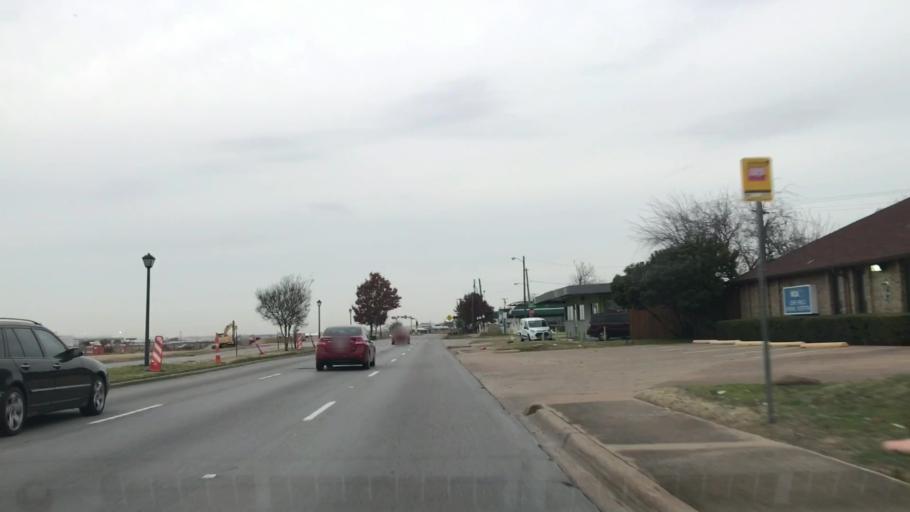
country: US
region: Texas
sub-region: Dallas County
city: University Park
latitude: 32.8376
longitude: -96.8326
